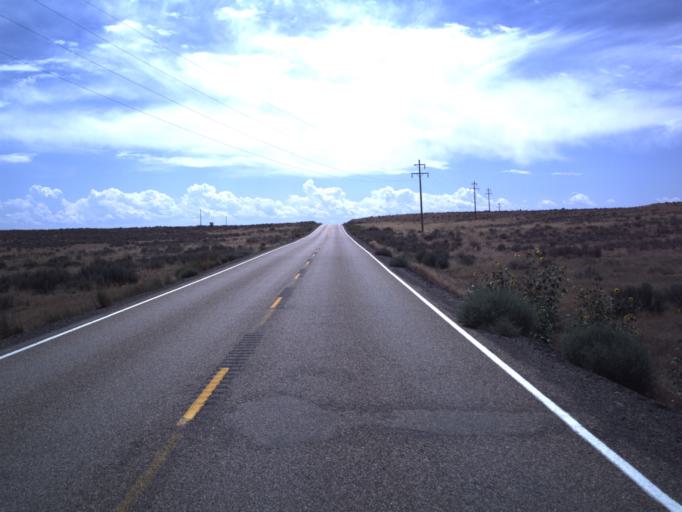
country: US
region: Utah
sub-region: Uintah County
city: Maeser
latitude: 40.2951
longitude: -109.6865
